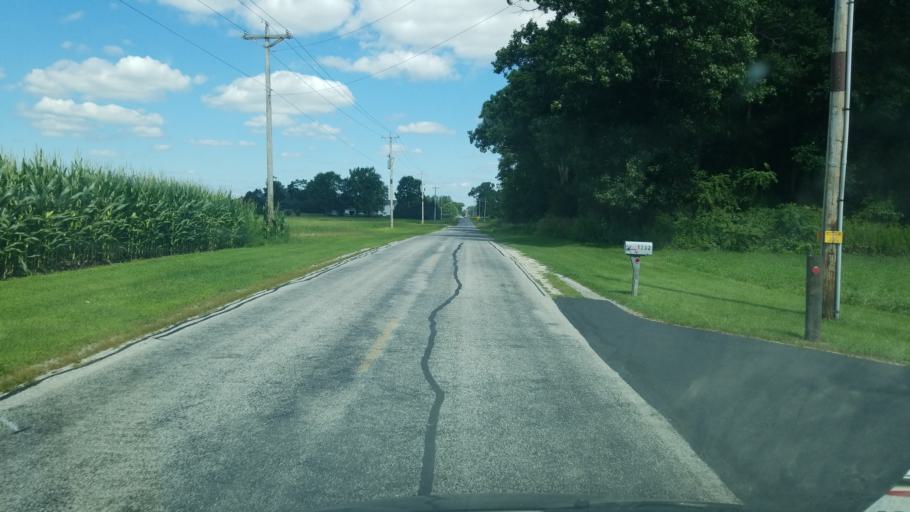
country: US
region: Ohio
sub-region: Fulton County
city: Swanton
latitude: 41.5477
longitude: -83.9408
